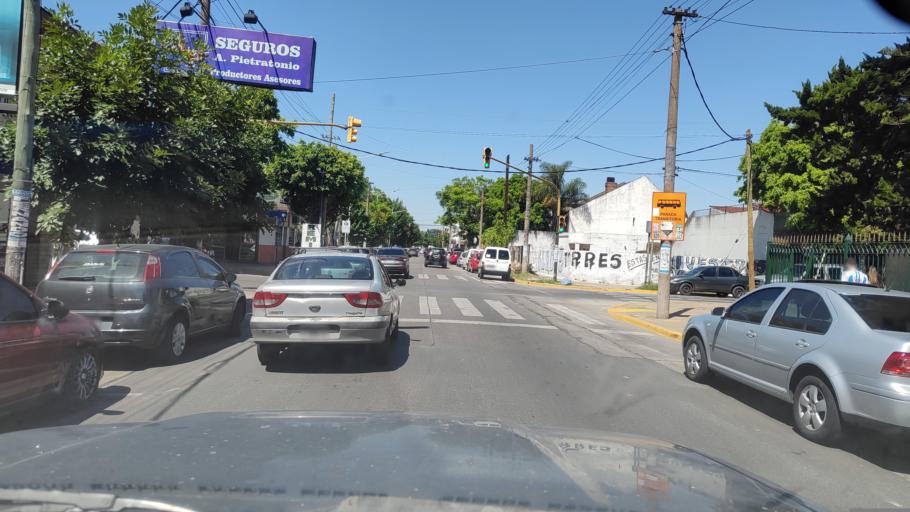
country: AR
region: Buenos Aires
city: San Justo
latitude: -34.6802
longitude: -58.5629
